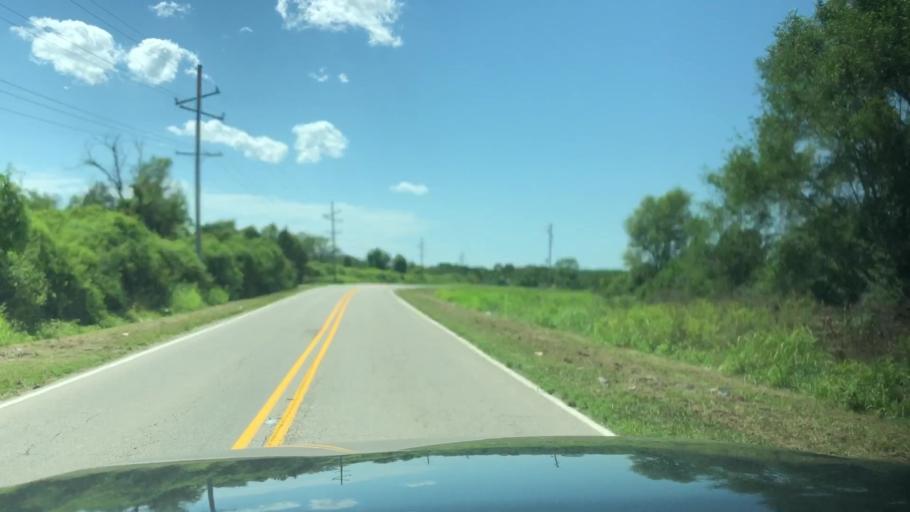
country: US
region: Illinois
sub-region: Saint Clair County
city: Alorton
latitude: 38.5530
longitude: -90.0781
